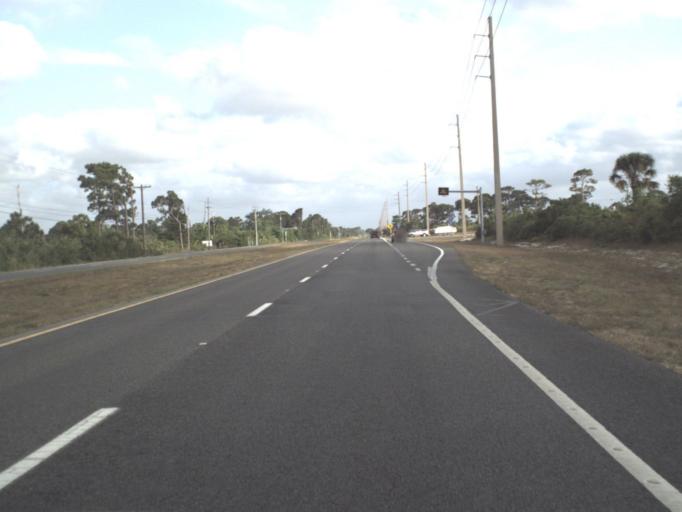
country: US
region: Florida
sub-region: Volusia County
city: Oak Hill
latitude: 28.7831
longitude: -80.8828
